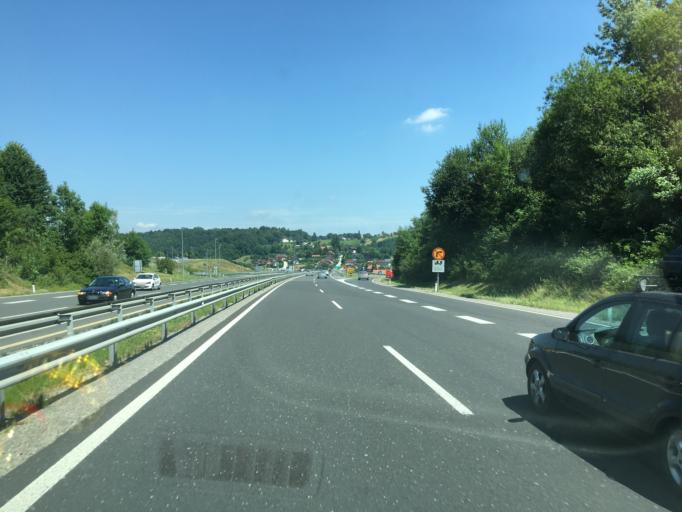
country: SI
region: Sentilj
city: Sentilj v Slov. Goricah
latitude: 46.6759
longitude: 15.6476
